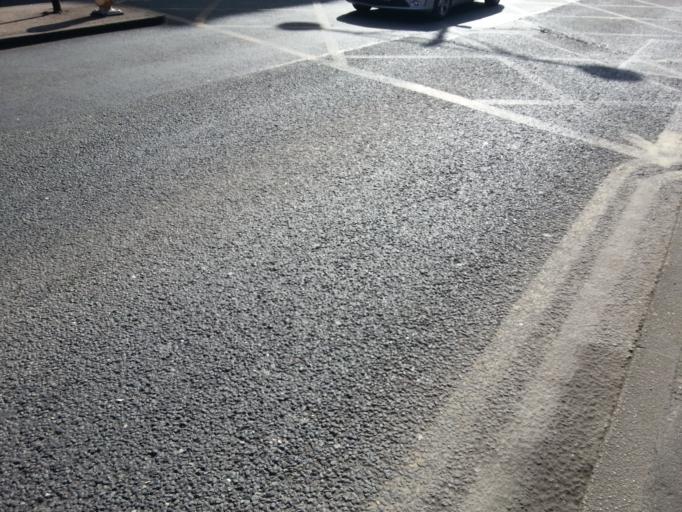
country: GB
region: England
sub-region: Manchester
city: Manchester
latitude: 53.4799
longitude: -2.2370
